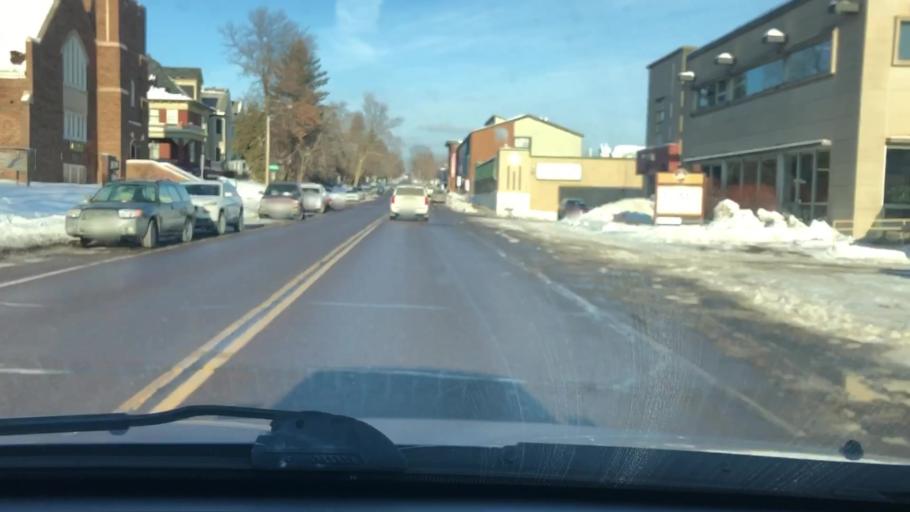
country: US
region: Minnesota
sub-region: Saint Louis County
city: Duluth
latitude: 46.7998
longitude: -92.0813
